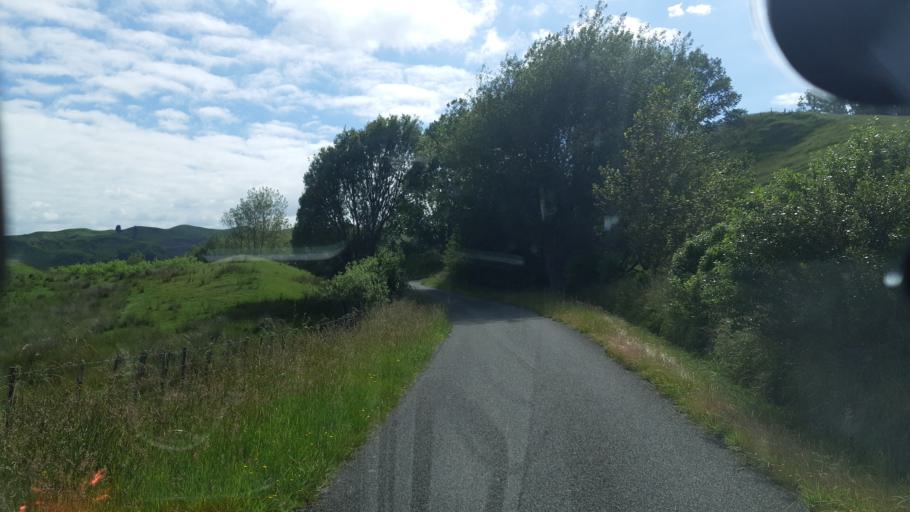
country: NZ
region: Manawatu-Wanganui
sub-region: Rangitikei District
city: Bulls
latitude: -39.9623
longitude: 175.4690
